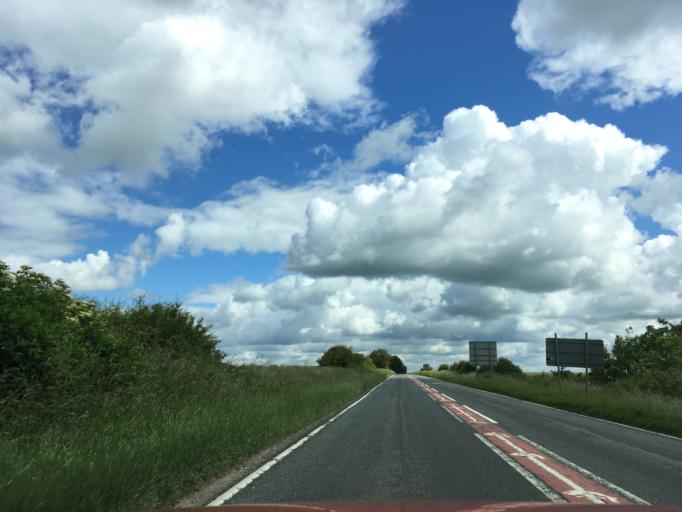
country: GB
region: England
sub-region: Oxfordshire
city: Shipton under Wychwood
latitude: 51.8378
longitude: -1.6052
